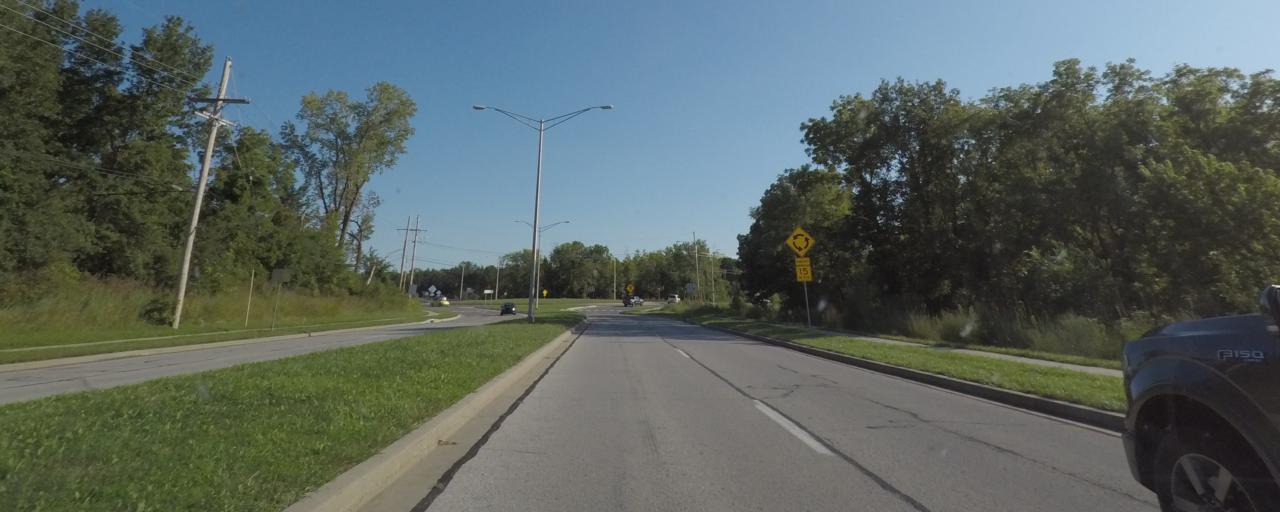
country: US
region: Missouri
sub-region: Clay County
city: Pleasant Valley
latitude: 39.2323
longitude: -94.4703
